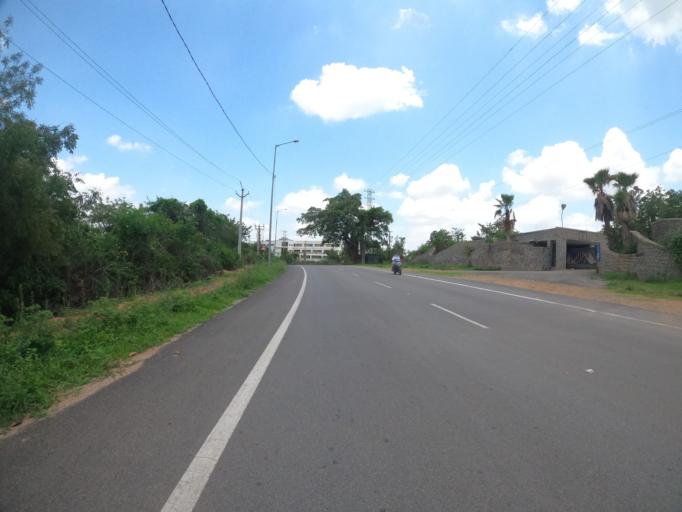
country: IN
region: Telangana
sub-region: Rangareddi
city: Sriramnagar
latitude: 17.3583
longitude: 78.3227
